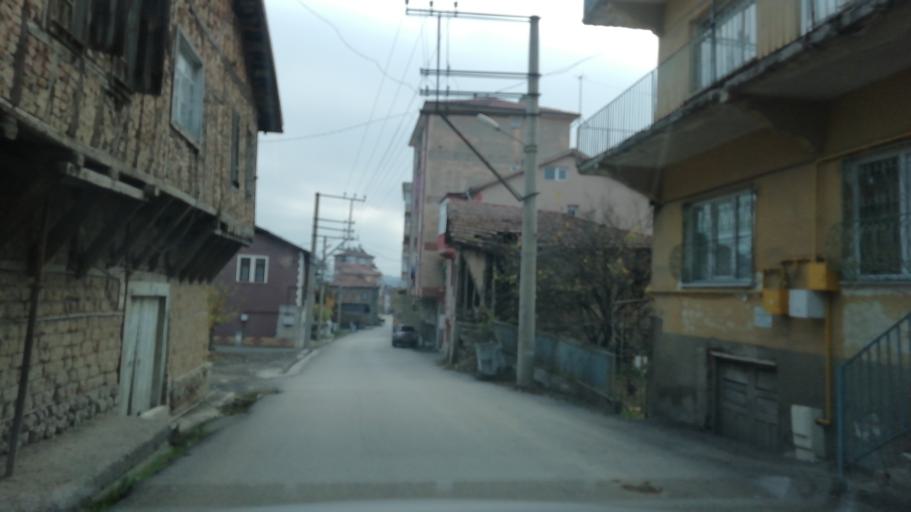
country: TR
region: Karabuk
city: Karabuk
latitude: 41.2215
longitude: 32.6271
